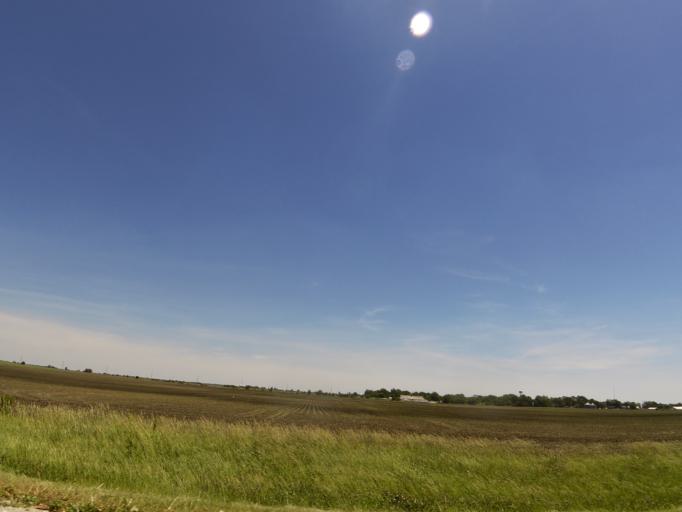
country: US
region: Illinois
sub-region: Vermilion County
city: Hoopeston
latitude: 40.5431
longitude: -87.6925
